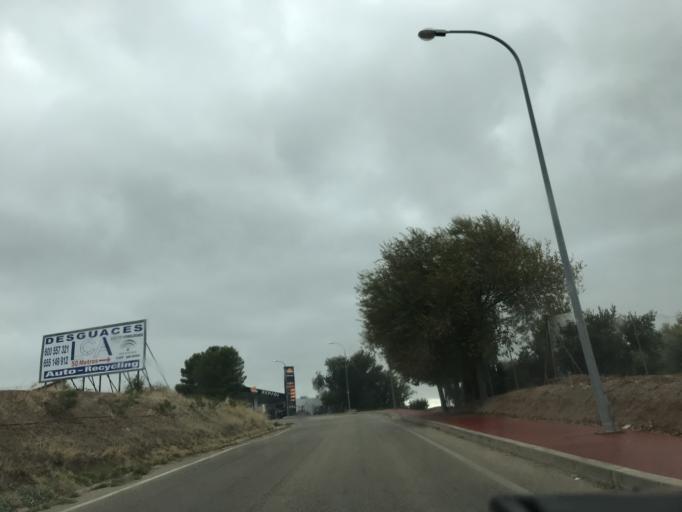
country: ES
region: Andalusia
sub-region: Provincia de Jaen
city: Peal de Becerro
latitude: 37.9169
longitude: -3.1319
